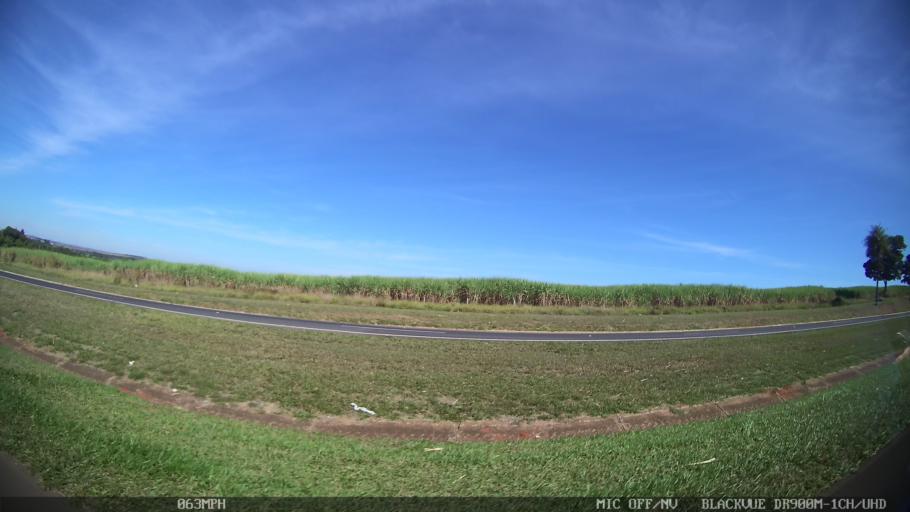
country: BR
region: Sao Paulo
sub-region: Porto Ferreira
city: Porto Ferreira
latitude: -21.8013
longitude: -47.5063
